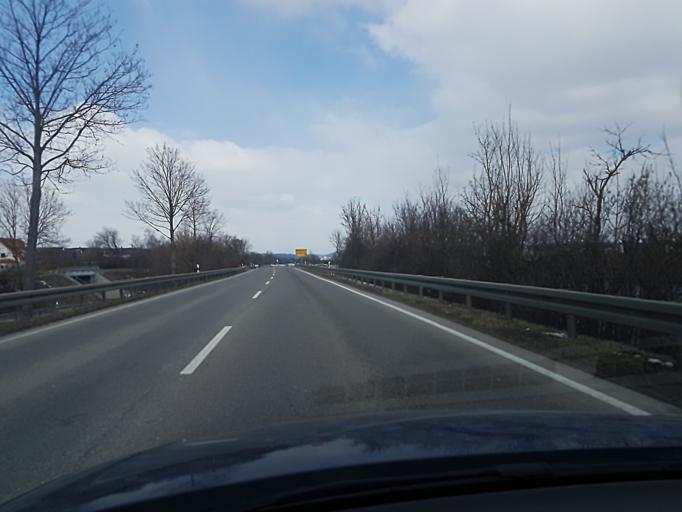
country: DE
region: Baden-Wuerttemberg
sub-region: Regierungsbezirk Stuttgart
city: Herrenberg
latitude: 48.5602
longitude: 8.8516
